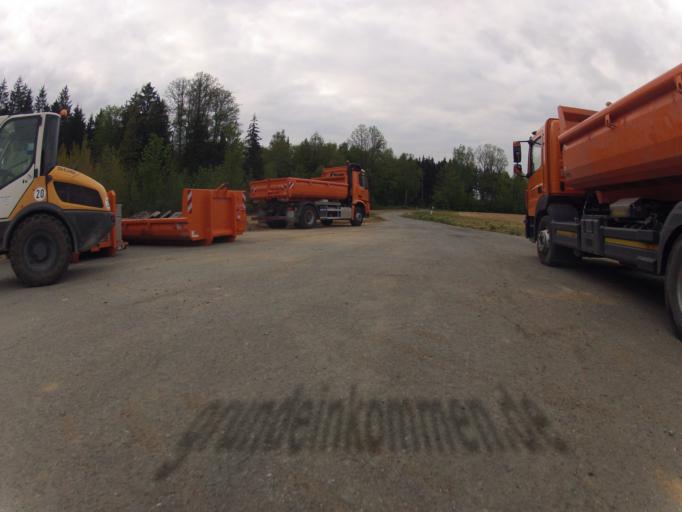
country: DE
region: Bavaria
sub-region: Upper Franconia
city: Sparneck
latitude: 50.1616
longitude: 11.8304
